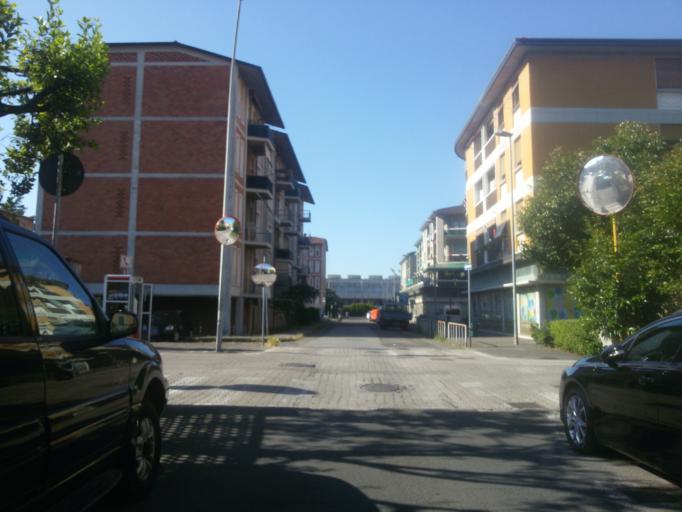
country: IT
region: Liguria
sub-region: Provincia di La Spezia
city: La Spezia
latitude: 44.1183
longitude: 9.8489
